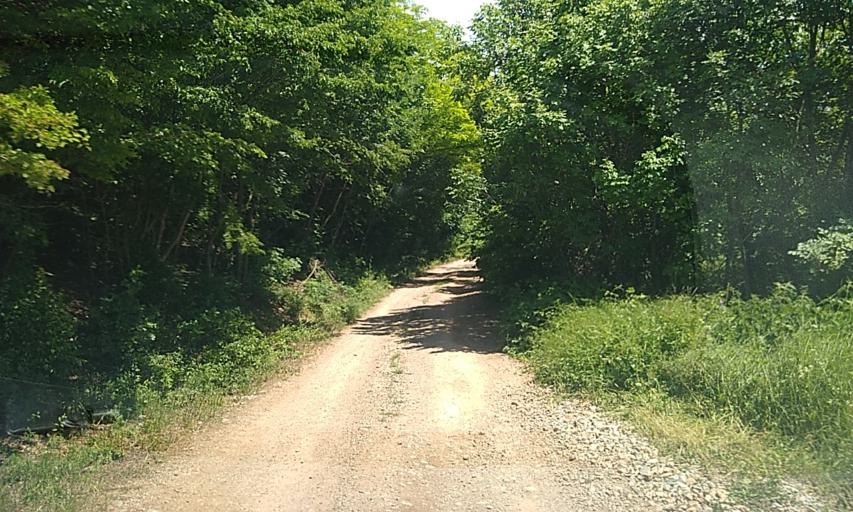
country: RS
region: Central Serbia
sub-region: Nisavski Okrug
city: Niska Banja
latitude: 43.3703
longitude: 21.9936
